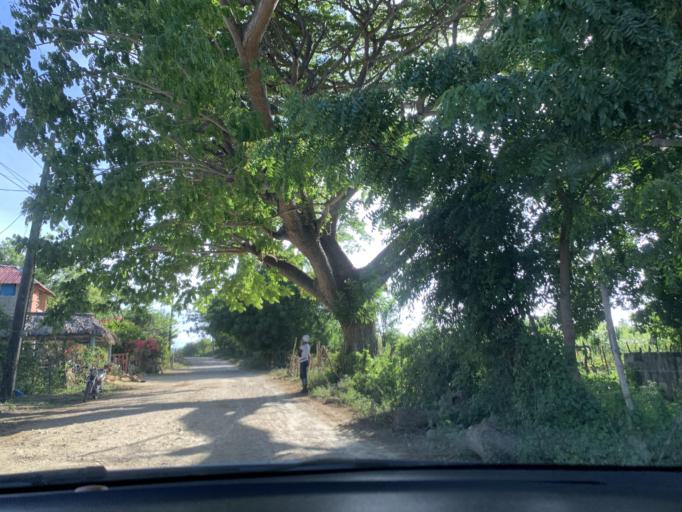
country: DO
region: Puerto Plata
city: Luperon
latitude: 19.8701
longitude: -70.9417
